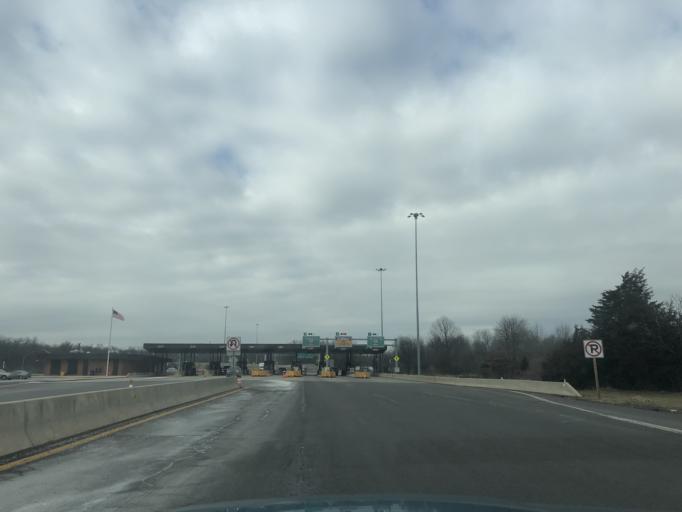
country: US
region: Pennsylvania
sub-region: Bucks County
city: Spinnerstown
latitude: 40.4361
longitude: -75.4214
